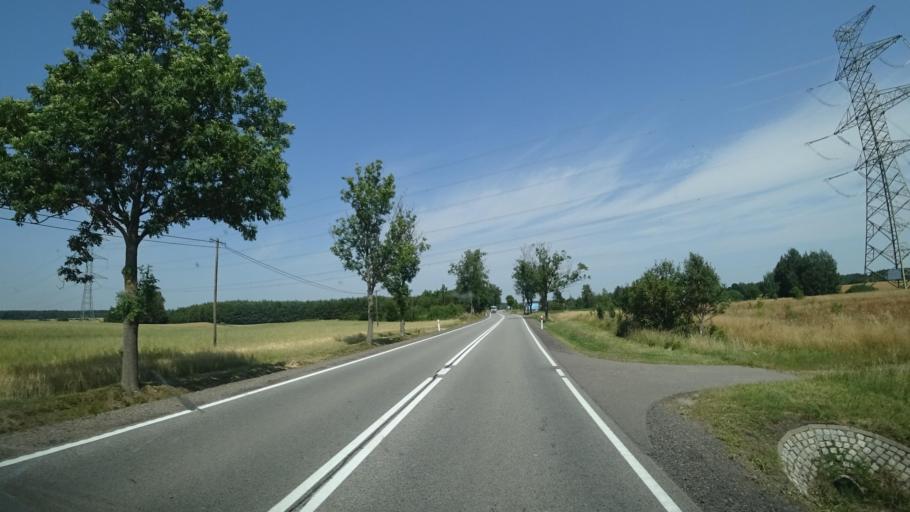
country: PL
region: Pomeranian Voivodeship
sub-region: Powiat koscierski
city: Koscierzyna
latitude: 54.1546
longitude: 18.0316
